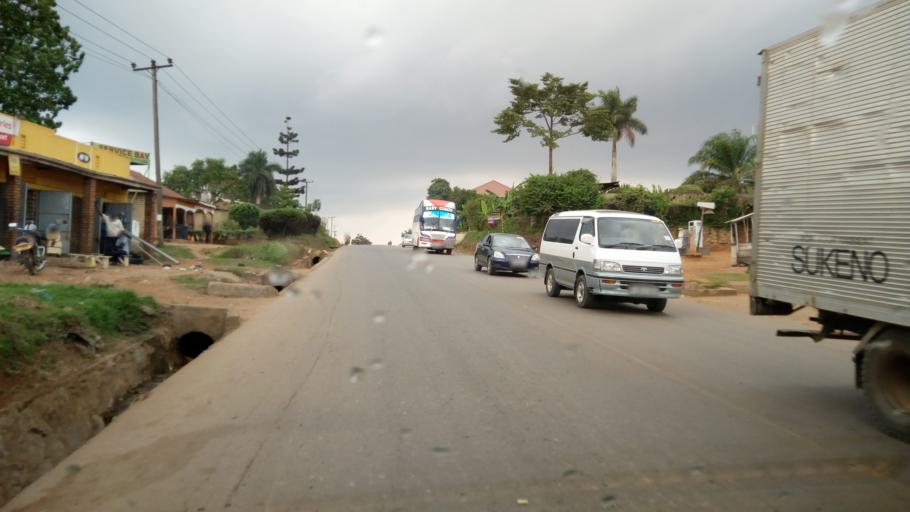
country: UG
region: Central Region
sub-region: Wakiso District
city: Wakiso
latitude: 0.4050
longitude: 32.5429
